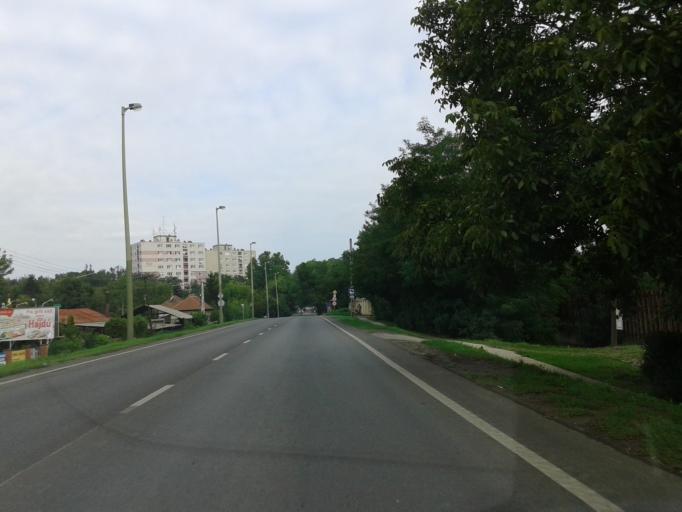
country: HU
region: Csongrad
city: Szeged
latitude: 46.2418
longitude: 20.1639
